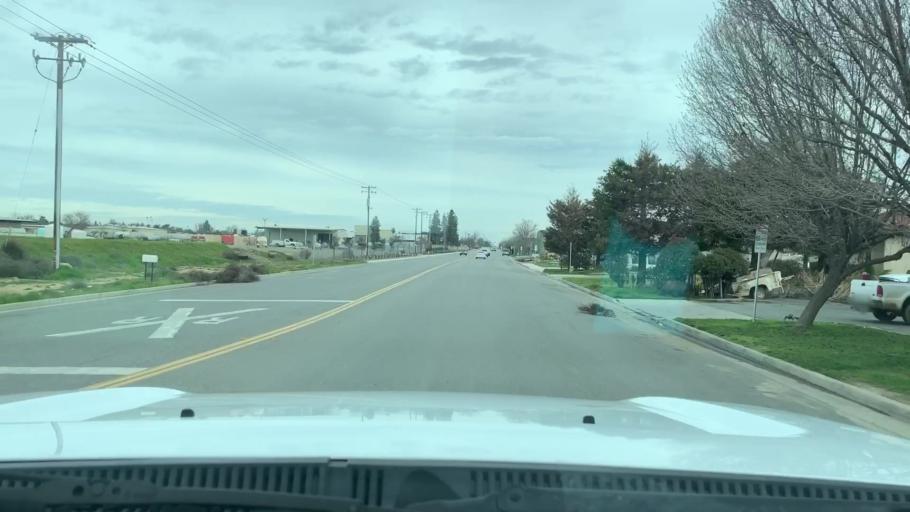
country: US
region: California
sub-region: Kern County
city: Shafter
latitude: 35.4932
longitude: -119.2606
